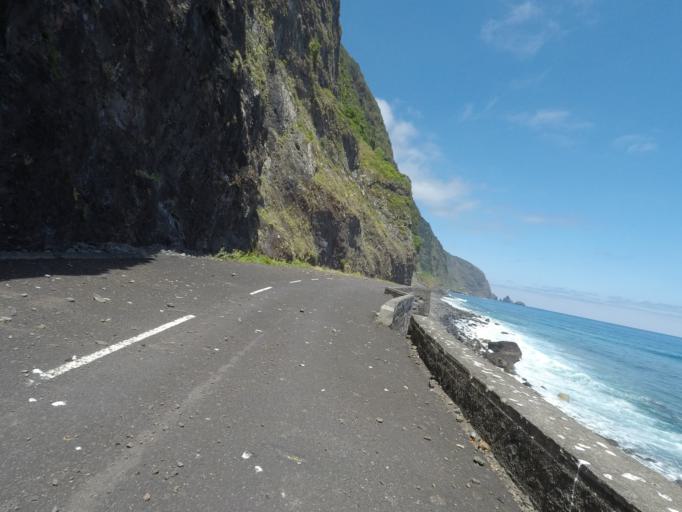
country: PT
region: Madeira
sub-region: Porto Moniz
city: Porto Moniz
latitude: 32.8273
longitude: -17.1250
